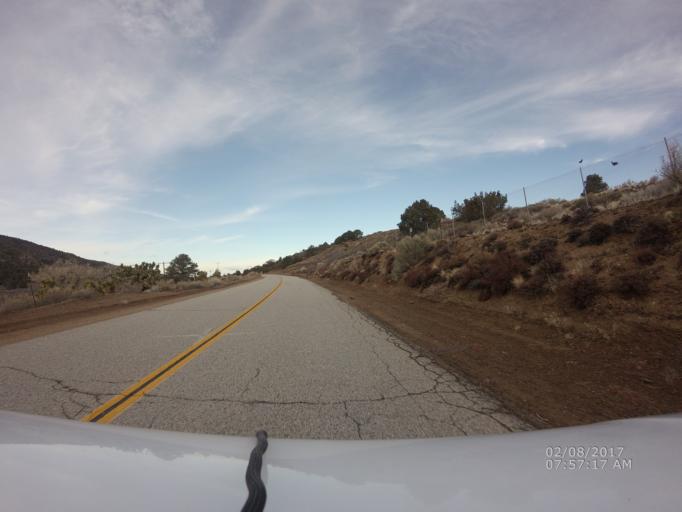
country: US
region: California
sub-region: San Bernardino County
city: Pinon Hills
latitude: 34.4148
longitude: -117.7776
